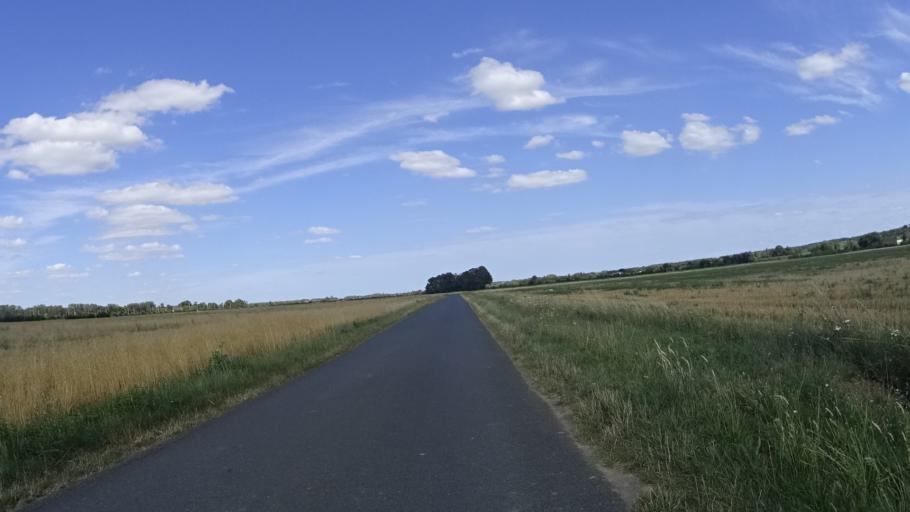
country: FR
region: Centre
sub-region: Departement d'Indre-et-Loire
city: Nazelles-Negron
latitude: 47.4088
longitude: 0.9260
